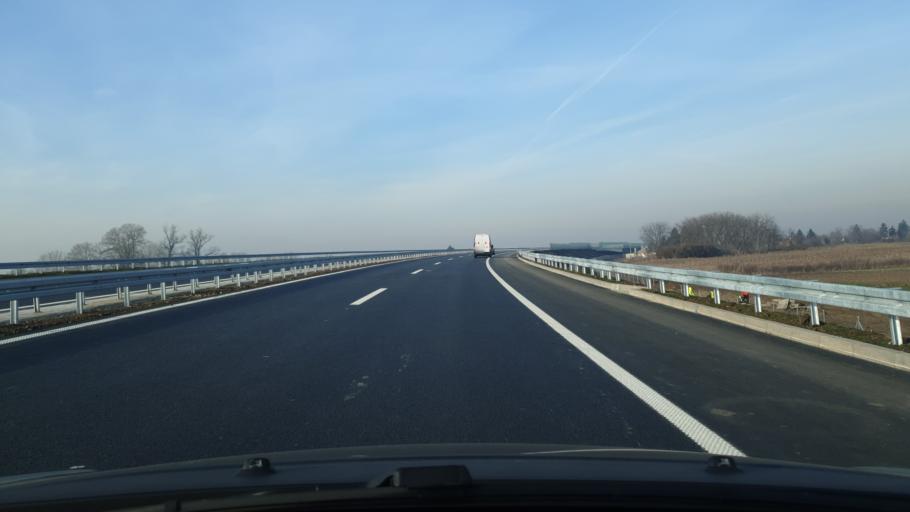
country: RS
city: Boljevci
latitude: 44.7294
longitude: 20.2476
